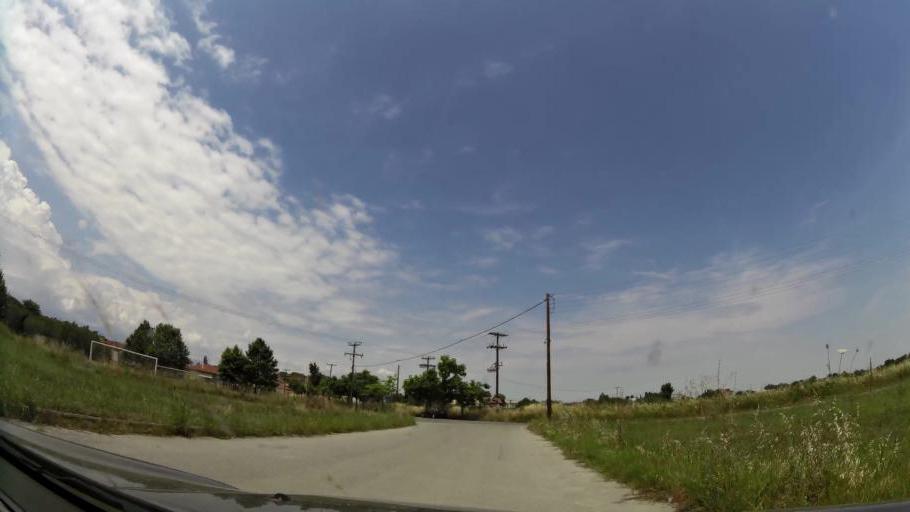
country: GR
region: Central Macedonia
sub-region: Nomos Pierias
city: Peristasi
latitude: 40.2641
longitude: 22.5360
